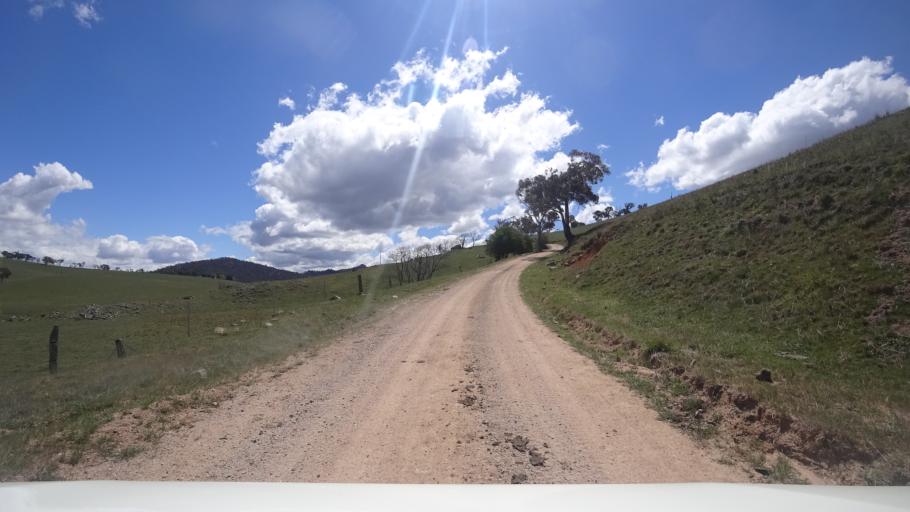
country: AU
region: New South Wales
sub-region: Oberon
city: Oberon
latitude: -33.5751
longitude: 149.9413
